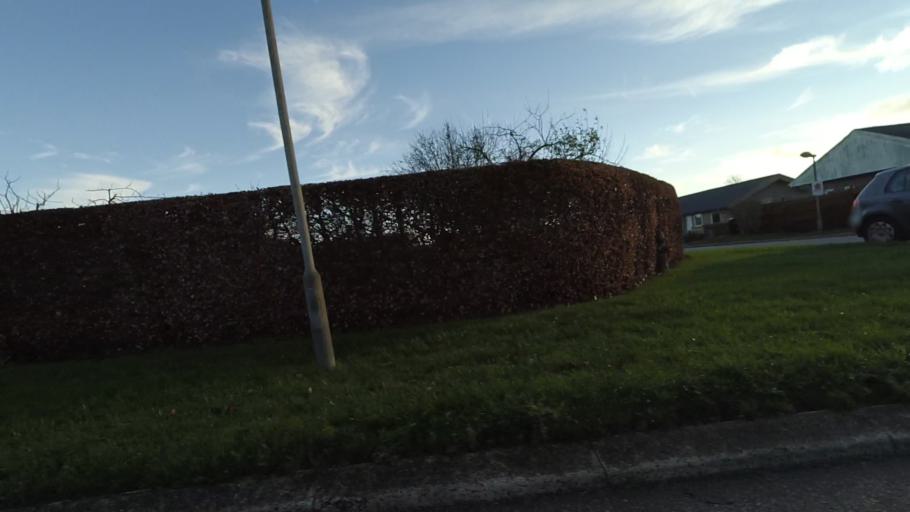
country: DK
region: Central Jutland
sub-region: Arhus Kommune
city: Arhus
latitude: 56.1131
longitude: 10.1820
